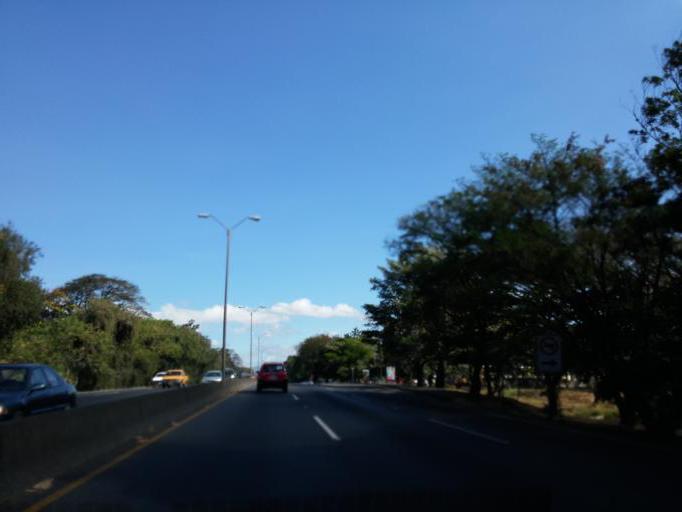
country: CR
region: Heredia
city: San Francisco
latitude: 9.9701
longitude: -84.1397
